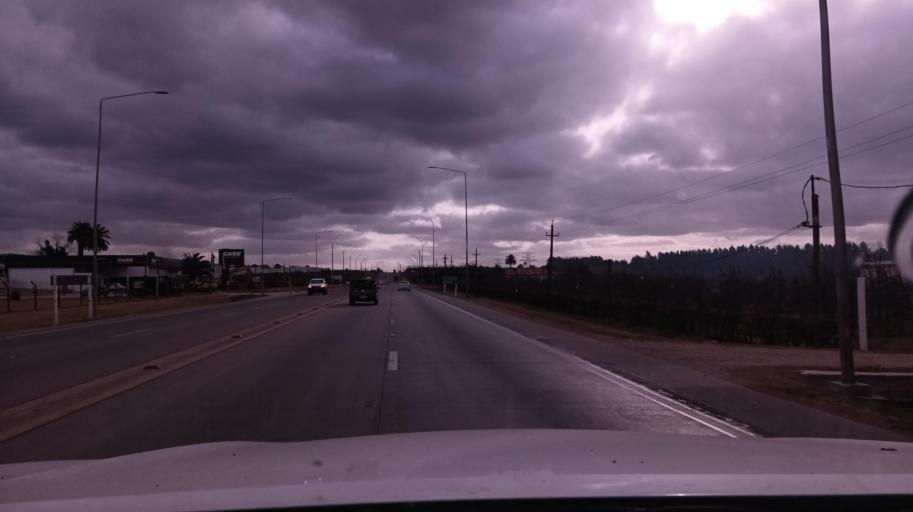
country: UY
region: Canelones
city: La Paz
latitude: -34.7931
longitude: -56.2065
